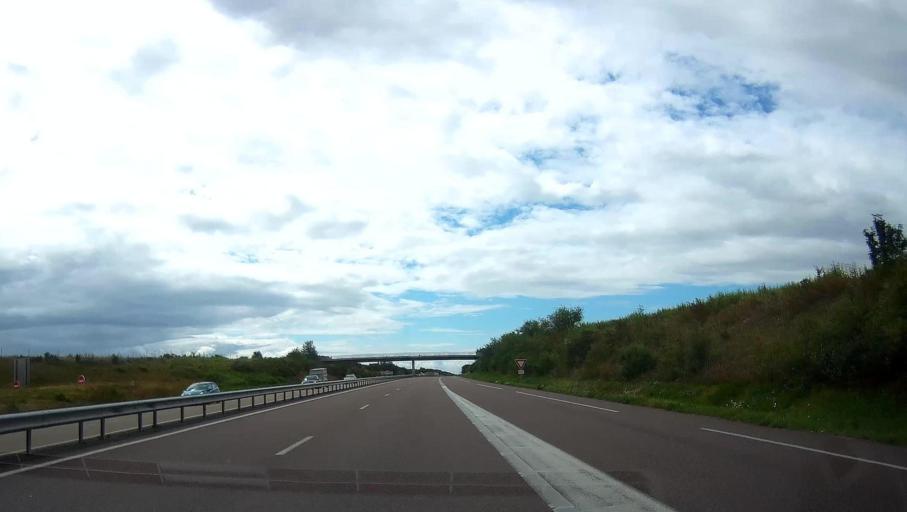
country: FR
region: Champagne-Ardenne
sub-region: Departement de l'Aube
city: Creney-pres-Troyes
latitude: 48.3292
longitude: 4.1670
